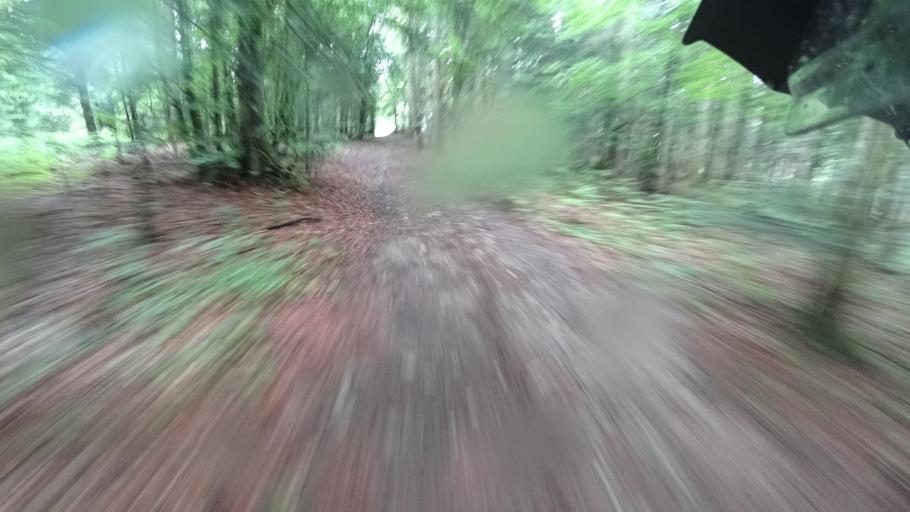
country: HR
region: Primorsko-Goranska
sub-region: Grad Delnice
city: Delnice
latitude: 45.3609
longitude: 14.8932
